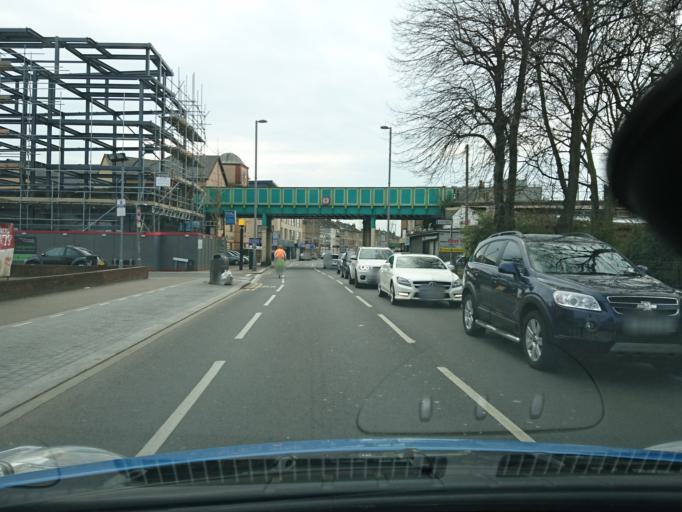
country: GB
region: England
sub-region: Greater London
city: Walthamstow
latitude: 51.5742
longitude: -0.0144
